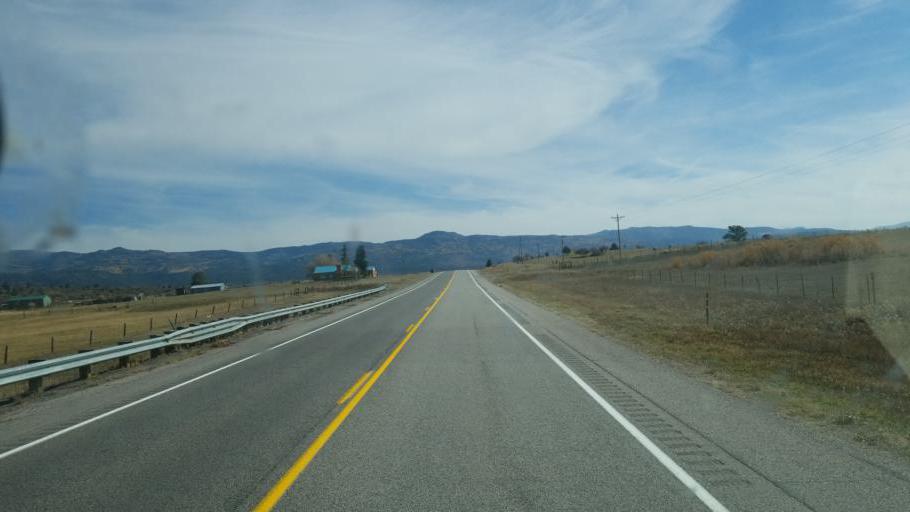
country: US
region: New Mexico
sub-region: Rio Arriba County
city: Chama
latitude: 36.8875
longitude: -106.6219
